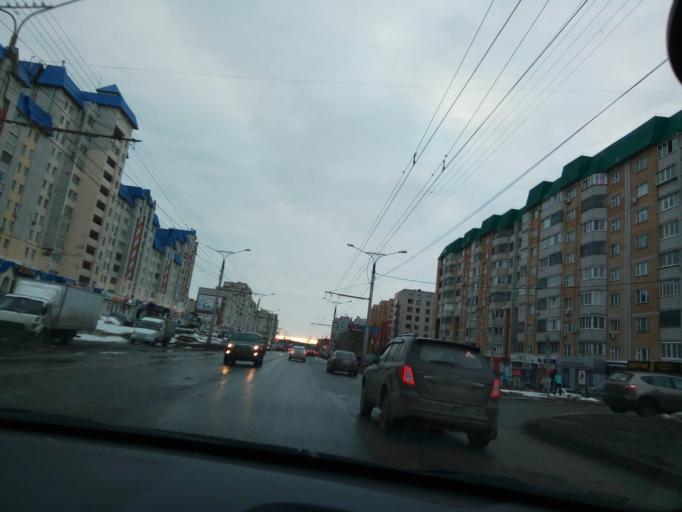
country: RU
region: Chuvashia
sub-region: Cheboksarskiy Rayon
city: Cheboksary
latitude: 56.1488
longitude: 47.1814
